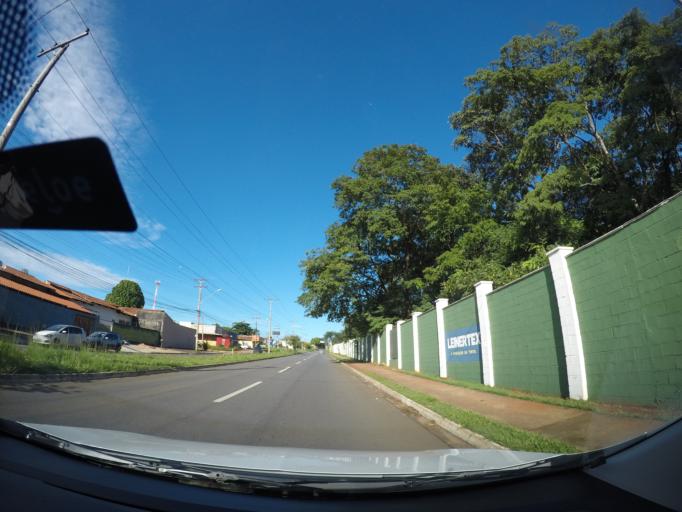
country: BR
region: Goias
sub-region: Goiania
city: Goiania
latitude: -16.7321
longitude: -49.2969
